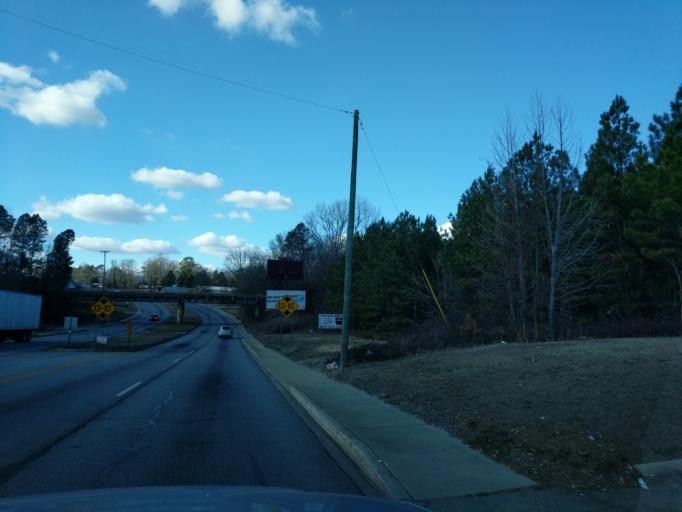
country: US
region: South Carolina
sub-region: Greenwood County
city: Greenwood
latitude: 34.2041
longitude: -82.1364
